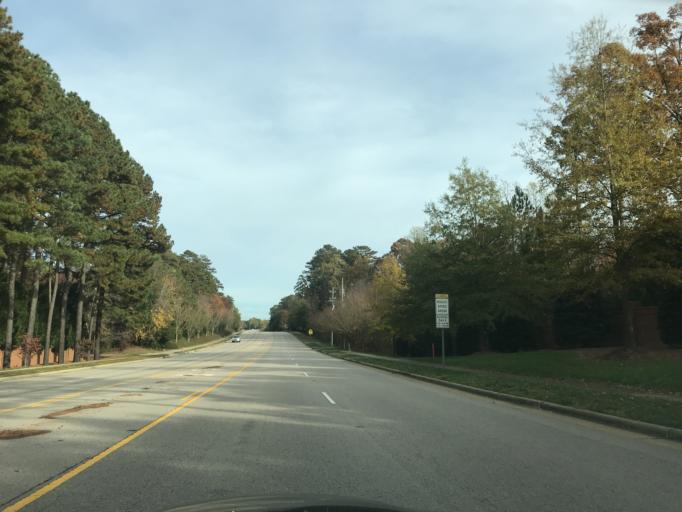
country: US
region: North Carolina
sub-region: Wake County
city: West Raleigh
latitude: 35.9020
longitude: -78.6707
